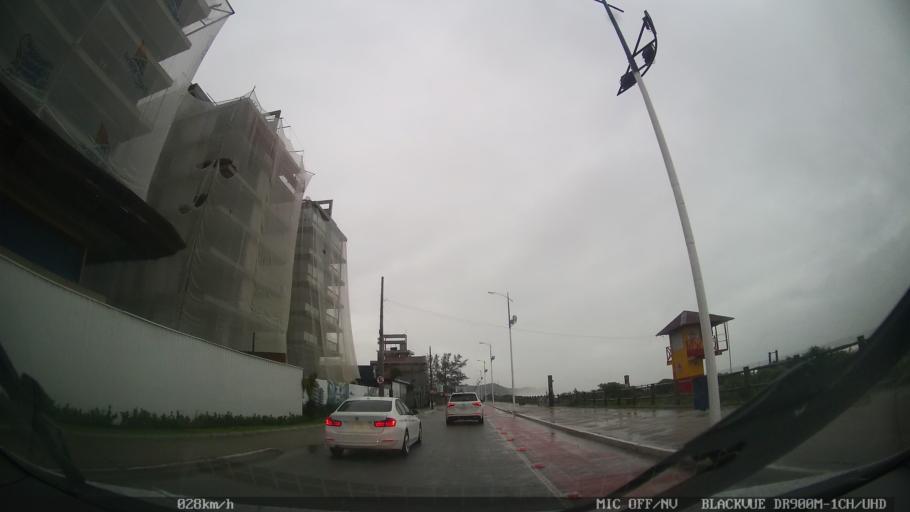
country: BR
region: Santa Catarina
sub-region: Balneario Camboriu
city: Balneario Camboriu
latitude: -26.9488
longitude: -48.6294
